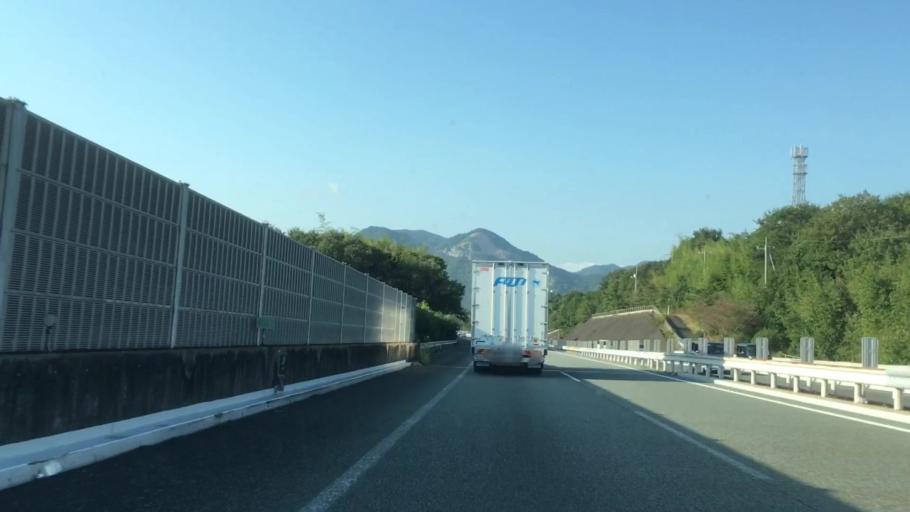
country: JP
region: Yamaguchi
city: Hofu
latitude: 34.0629
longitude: 131.5019
